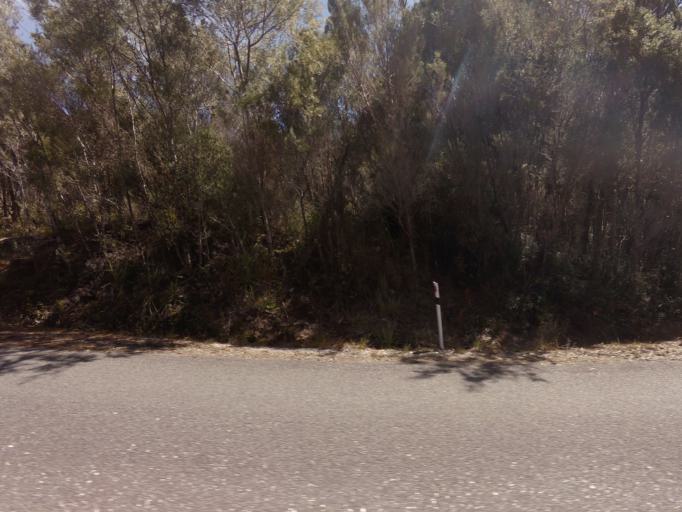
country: AU
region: Tasmania
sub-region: West Coast
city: Queenstown
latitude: -42.7699
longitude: 146.0436
